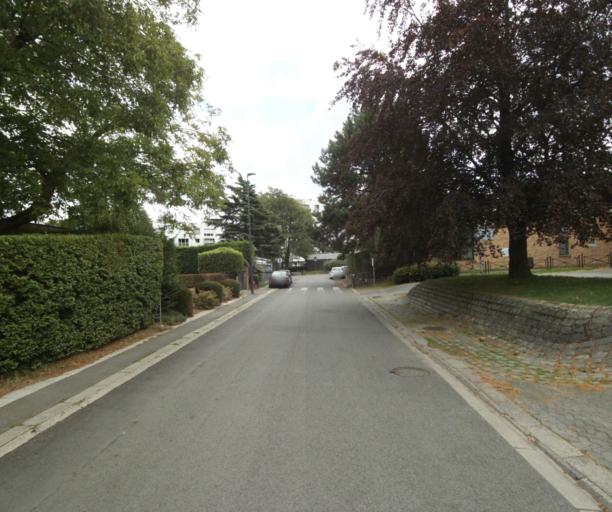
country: FR
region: Nord-Pas-de-Calais
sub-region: Departement du Nord
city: Villeneuve-d'Ascq
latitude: 50.6172
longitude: 3.1433
